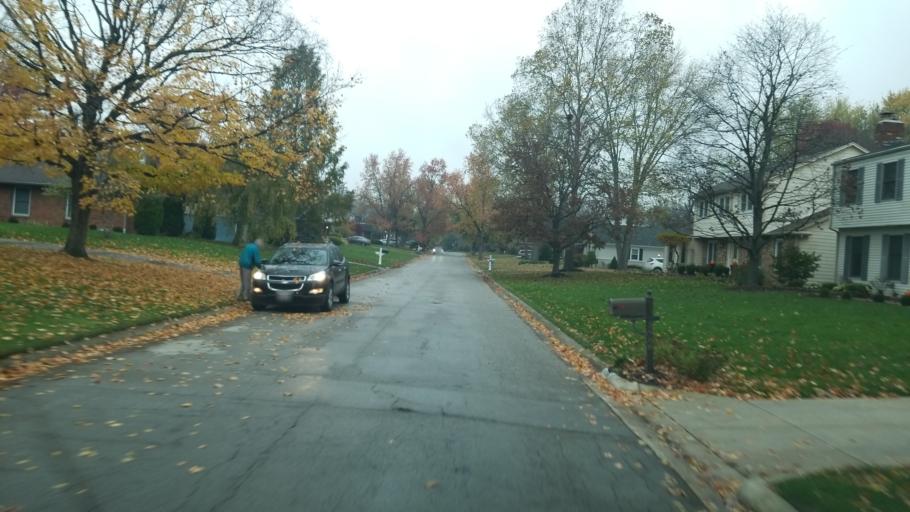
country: US
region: Ohio
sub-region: Franklin County
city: Worthington
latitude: 40.0814
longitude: -83.0467
